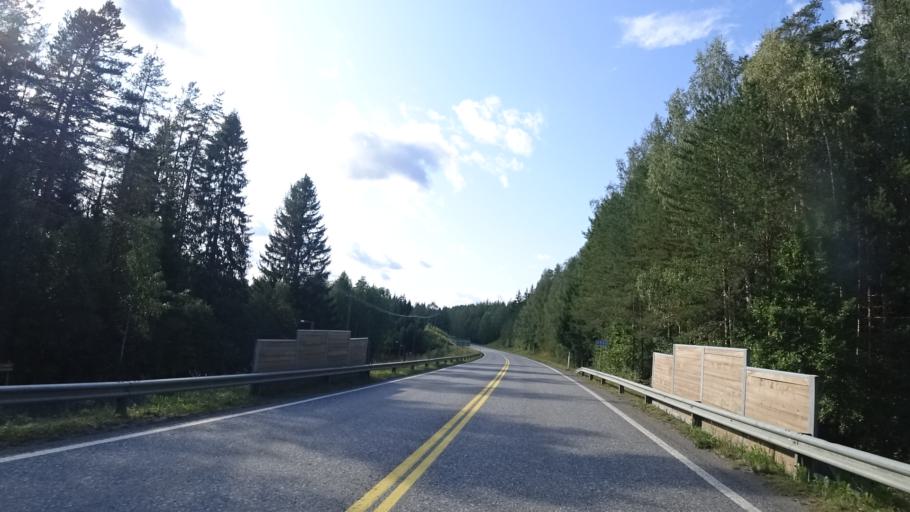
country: FI
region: North Karelia
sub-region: Keski-Karjala
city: Kitee
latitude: 62.0876
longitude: 30.1365
